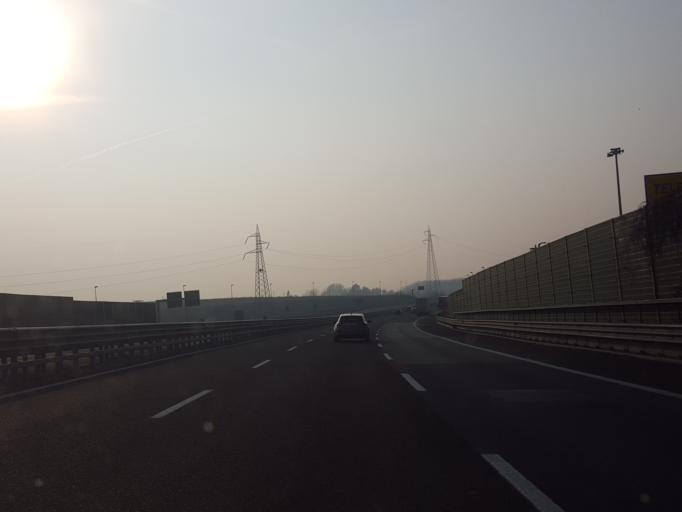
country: IT
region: Veneto
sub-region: Provincia di Venezia
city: Marano
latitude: 45.4779
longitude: 12.1279
